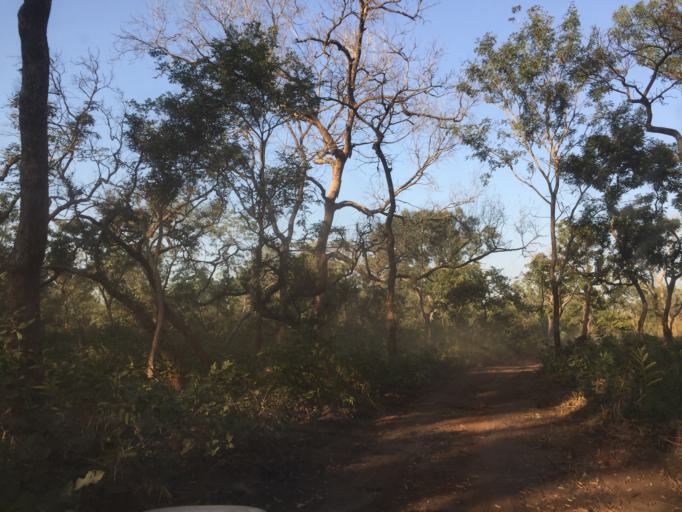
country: GW
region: Oio
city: Farim
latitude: 12.5281
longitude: -15.2788
